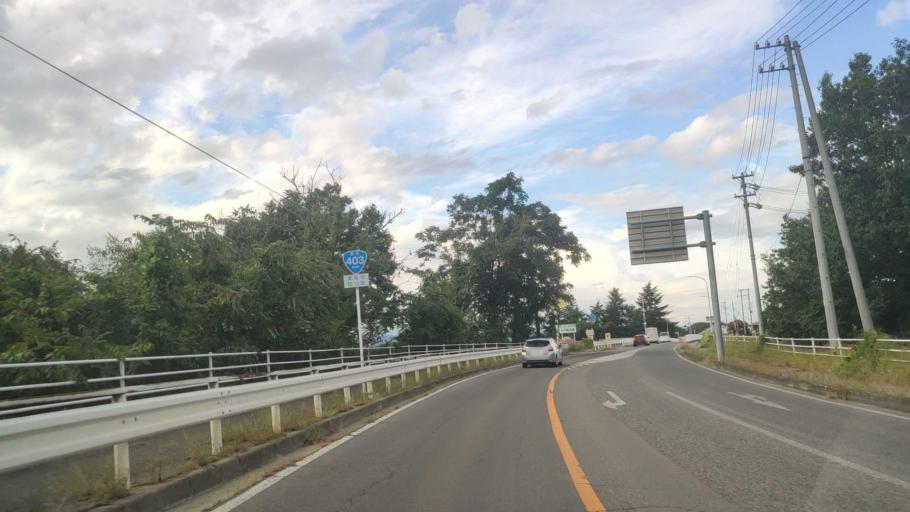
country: JP
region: Nagano
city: Suzaka
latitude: 36.6871
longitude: 138.3154
